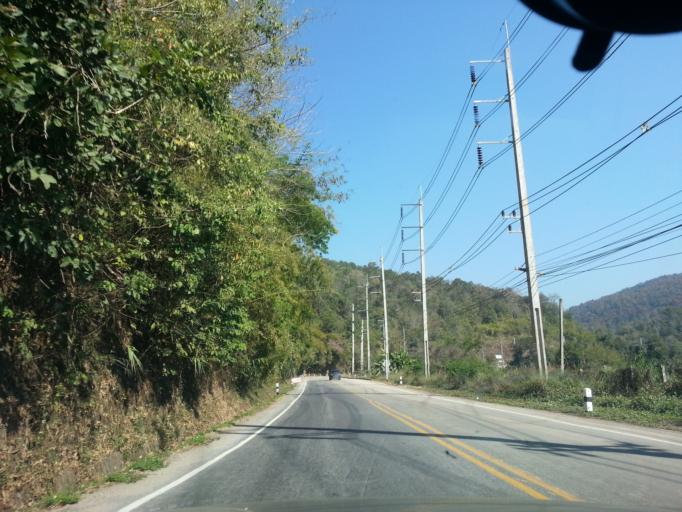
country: TH
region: Chiang Mai
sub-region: Amphoe Chiang Dao
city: Chiang Dao
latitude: 19.2534
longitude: 98.9678
